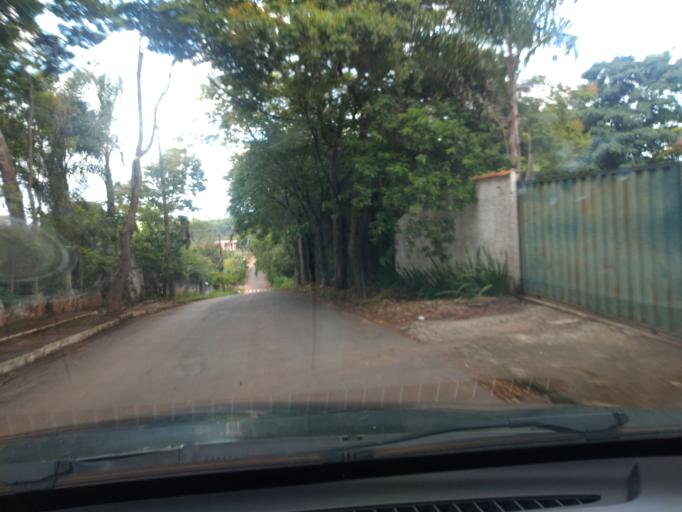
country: BR
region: Minas Gerais
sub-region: Tres Coracoes
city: Tres Coracoes
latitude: -21.6884
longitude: -45.2700
